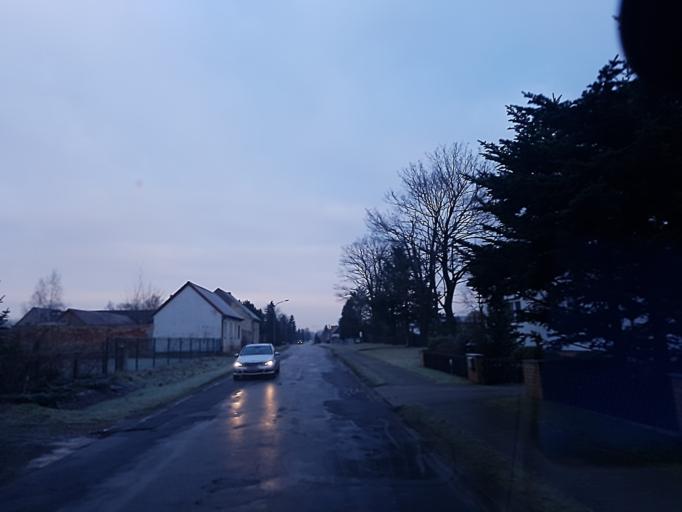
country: DE
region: Brandenburg
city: Finsterwalde
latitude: 51.6571
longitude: 13.7117
